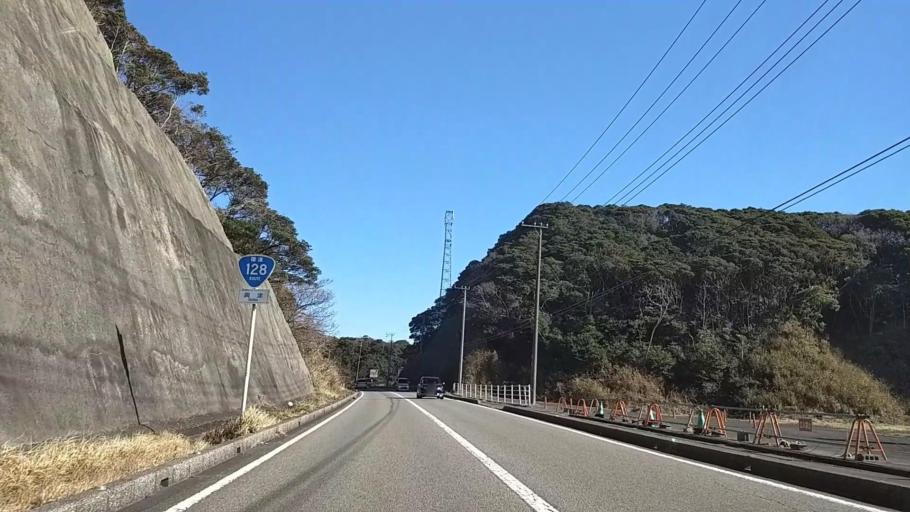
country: JP
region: Chiba
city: Katsuura
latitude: 35.1403
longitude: 140.2536
